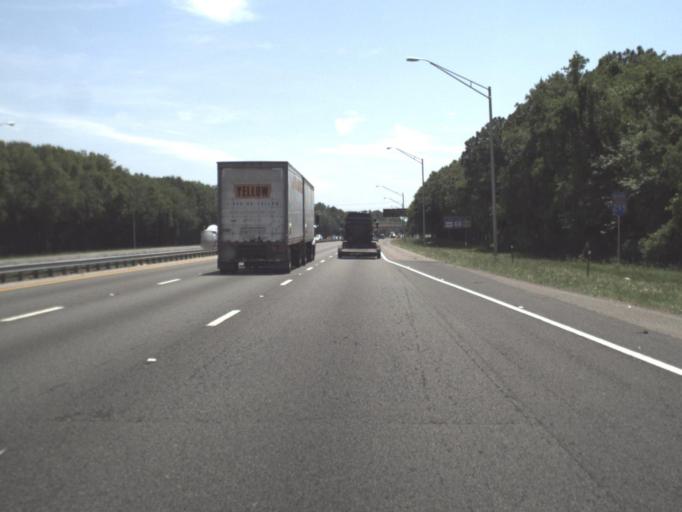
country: US
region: Florida
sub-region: Clay County
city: Bellair-Meadowbrook Terrace
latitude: 30.2642
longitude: -81.7653
